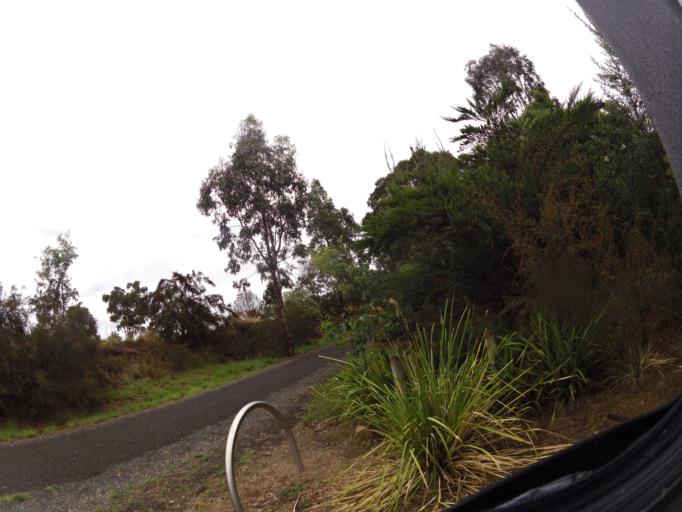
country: AU
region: Victoria
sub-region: East Gippsland
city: Bairnsdale
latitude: -37.8140
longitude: 147.7358
